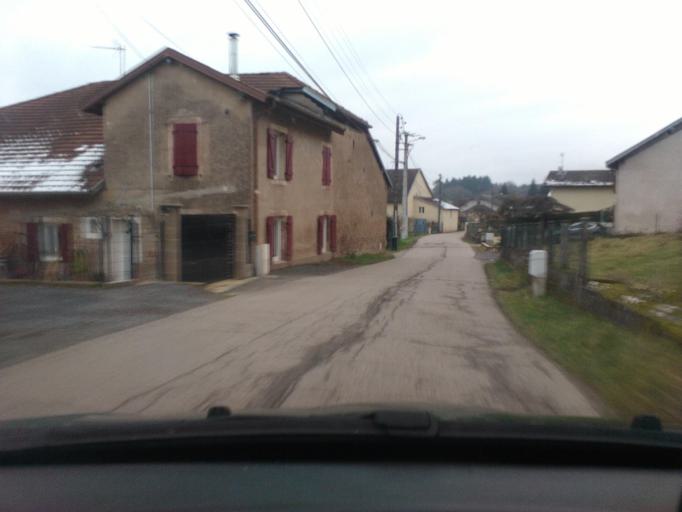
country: FR
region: Lorraine
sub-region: Departement des Vosges
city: Etival-Clairefontaine
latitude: 48.3597
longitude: 6.8689
